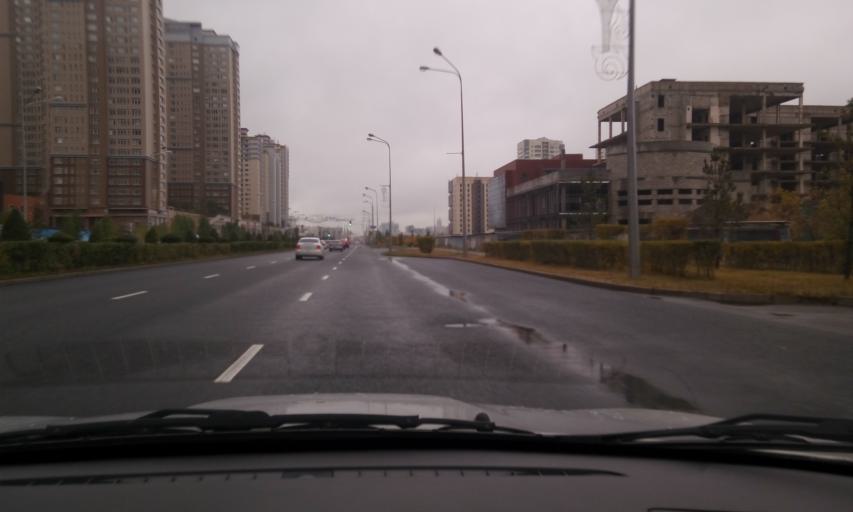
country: KZ
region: Astana Qalasy
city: Astana
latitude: 51.1282
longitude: 71.4670
